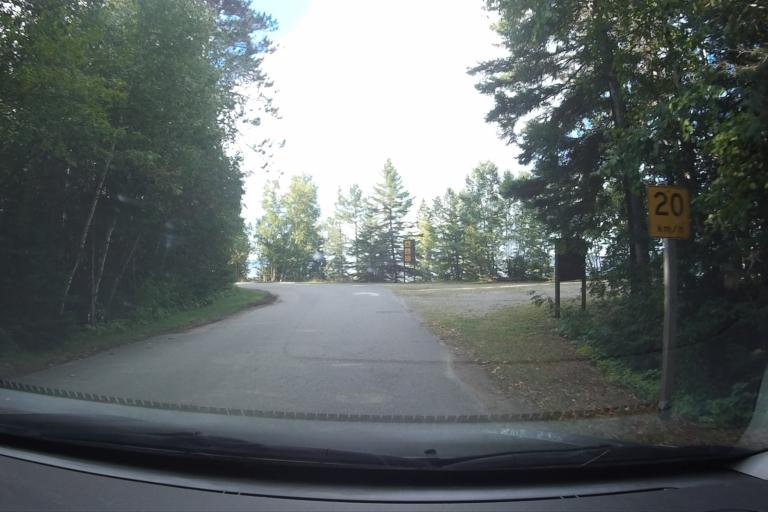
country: CA
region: Ontario
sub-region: Algoma
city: Sault Ste. Marie
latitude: 47.3328
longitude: -84.6155
